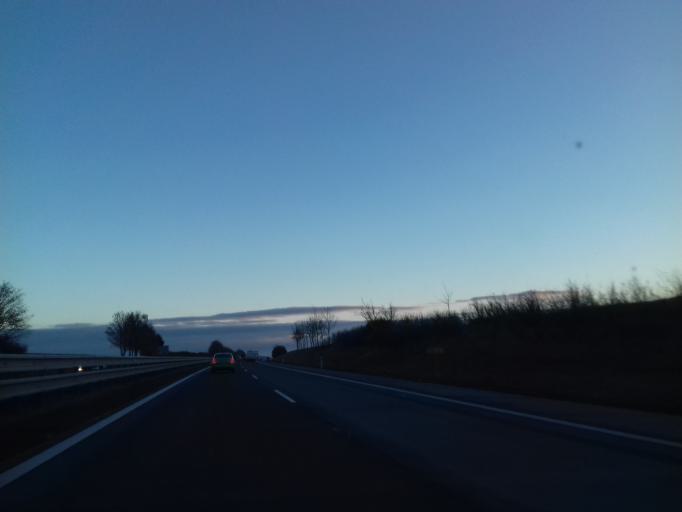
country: CZ
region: South Moravian
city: Drnovice
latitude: 49.2307
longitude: 16.9313
